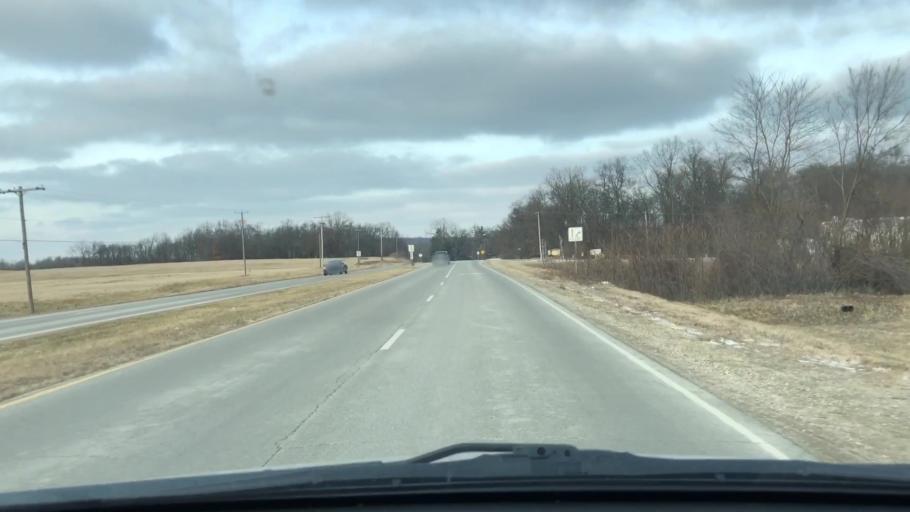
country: US
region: Indiana
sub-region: Steuben County
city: Angola
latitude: 41.6794
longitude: -85.0287
